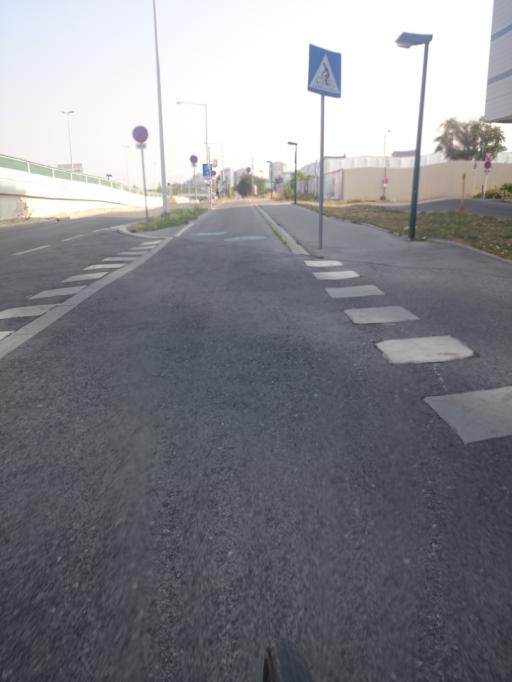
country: AT
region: Lower Austria
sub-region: Politischer Bezirk Korneuburg
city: Langenzersdorf
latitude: 48.2684
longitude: 16.3978
